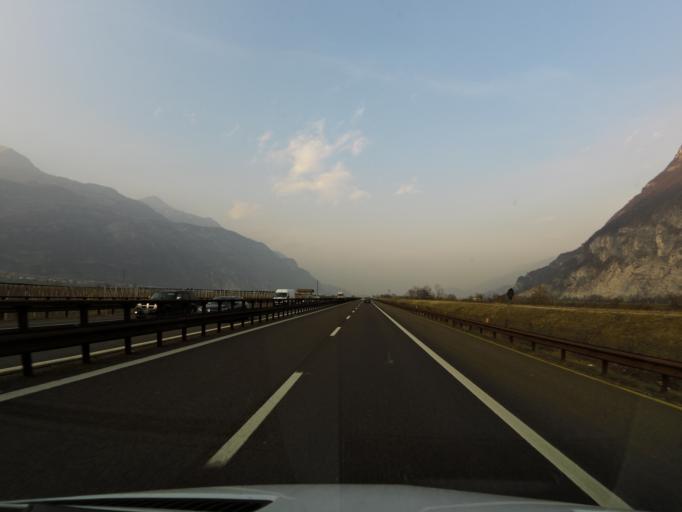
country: IT
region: Trentino-Alto Adige
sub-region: Provincia di Trento
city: Aldeno
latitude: 45.9670
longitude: 11.1070
